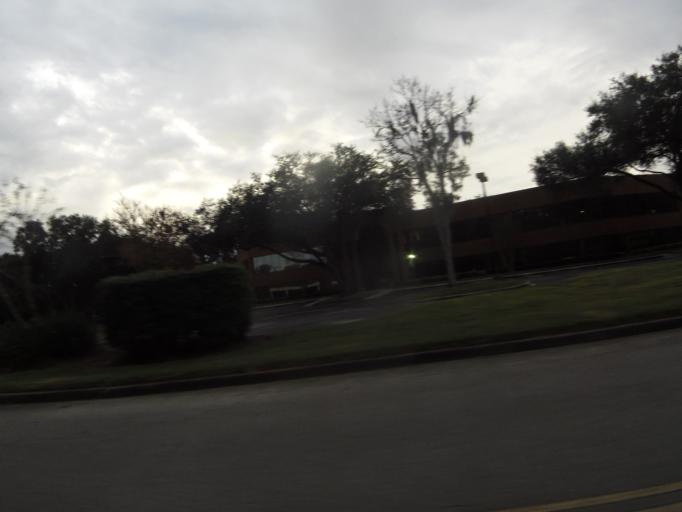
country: US
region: Florida
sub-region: Duval County
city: Jacksonville
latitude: 30.2421
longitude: -81.5797
